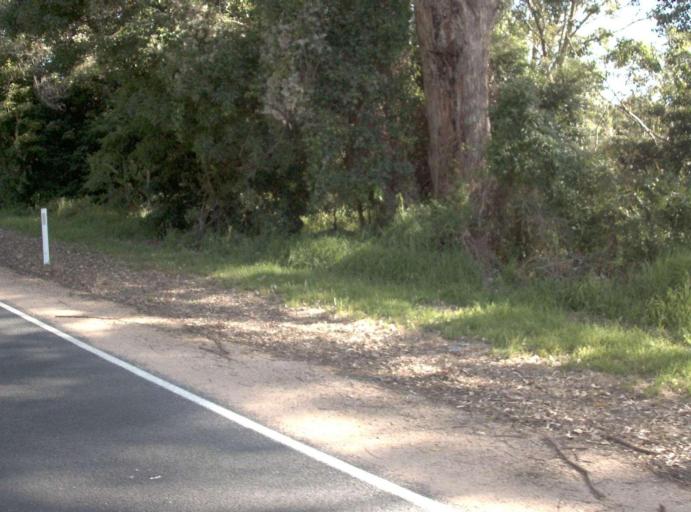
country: AU
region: Victoria
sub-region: East Gippsland
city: Lakes Entrance
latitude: -37.7158
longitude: 148.4559
